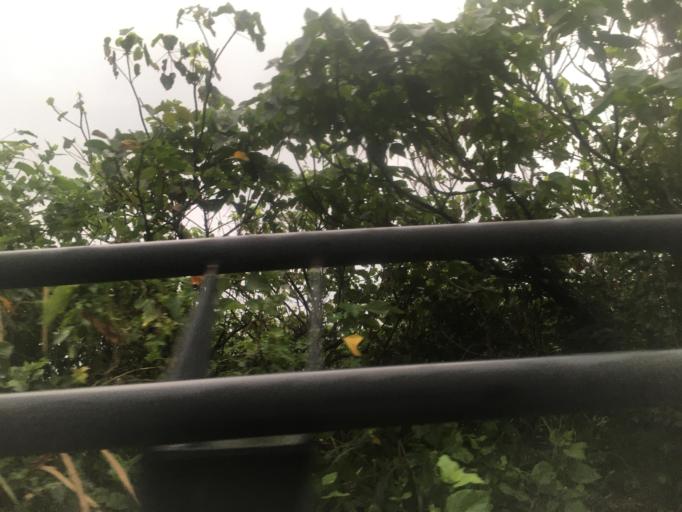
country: TW
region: Taiwan
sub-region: Keelung
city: Keelung
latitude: 25.0173
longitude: 121.9885
